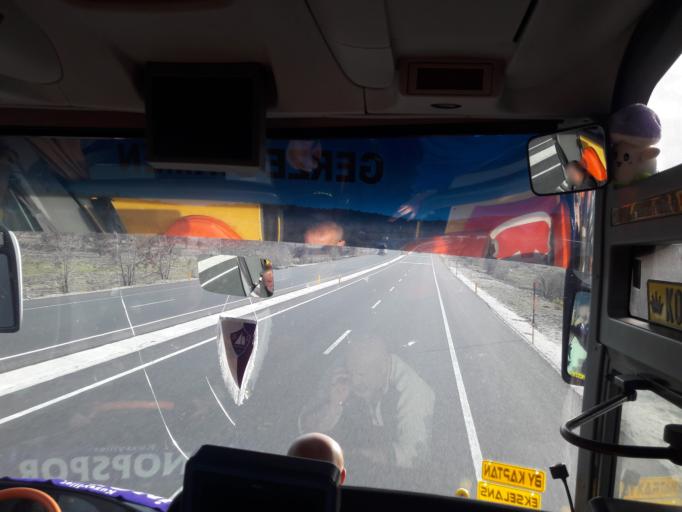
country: TR
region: Cankiri
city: Ilgaz
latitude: 40.8499
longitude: 33.6008
